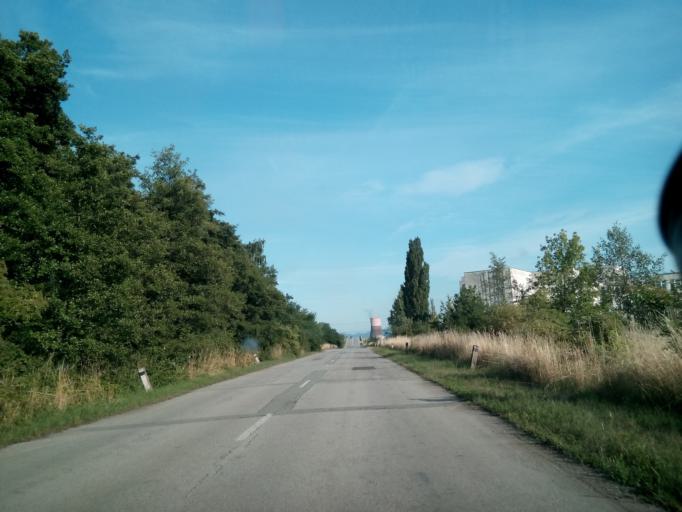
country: SK
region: Kosicky
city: Kosice
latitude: 48.6329
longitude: 21.1787
